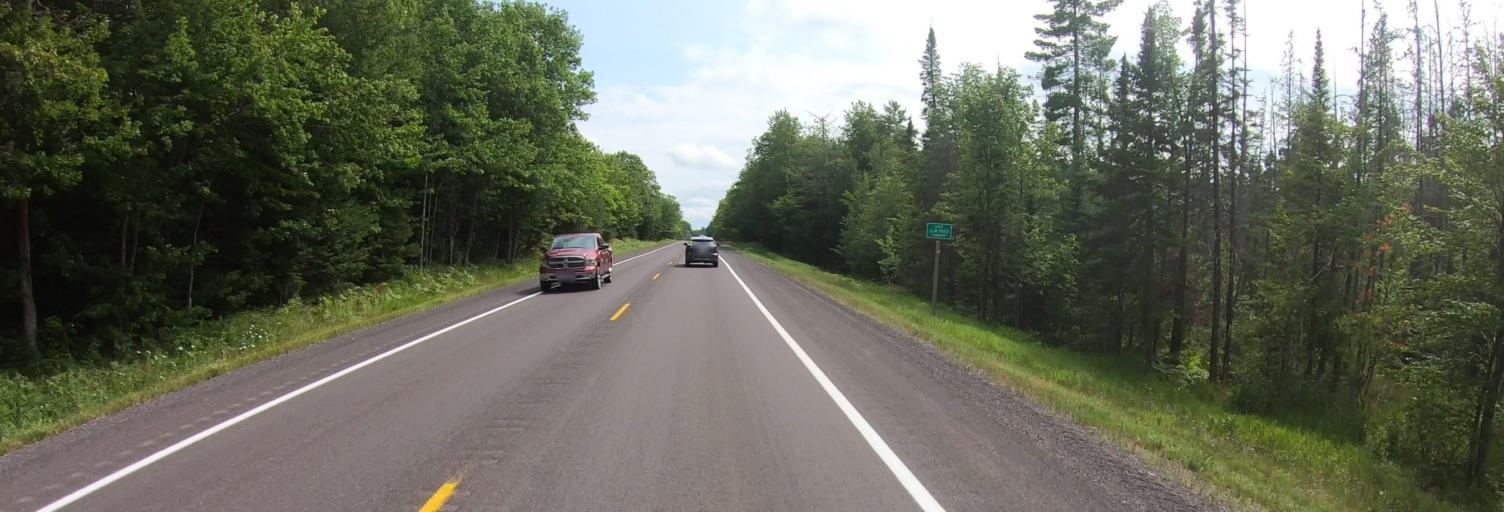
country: US
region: Michigan
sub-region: Houghton County
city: Hancock
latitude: 46.9810
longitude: -88.7809
